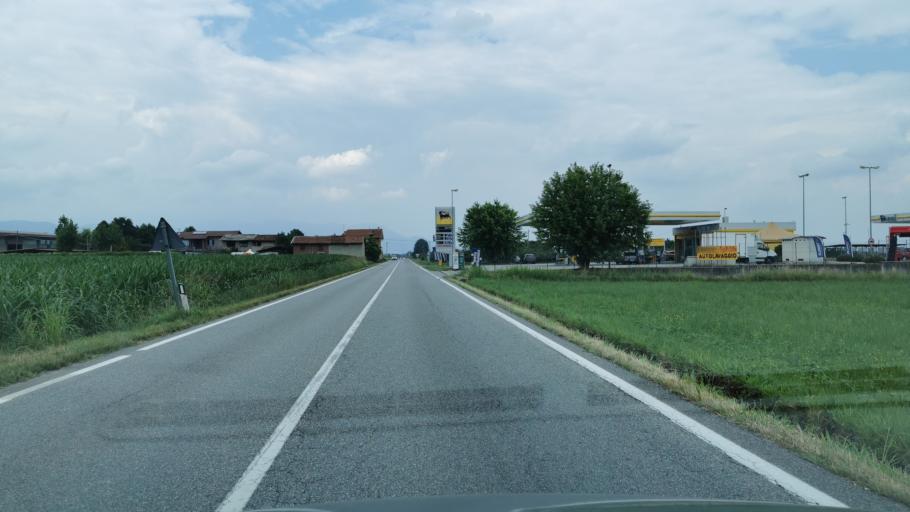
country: IT
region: Piedmont
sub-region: Provincia di Torino
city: Cavour
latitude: 44.8055
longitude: 7.3729
